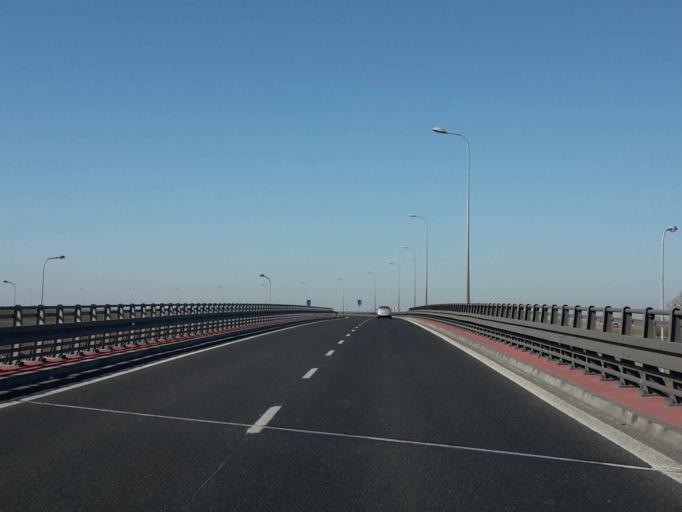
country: PL
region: Greater Poland Voivodeship
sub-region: Powiat gnieznienski
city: Lubowo
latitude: 52.5229
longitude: 17.5084
